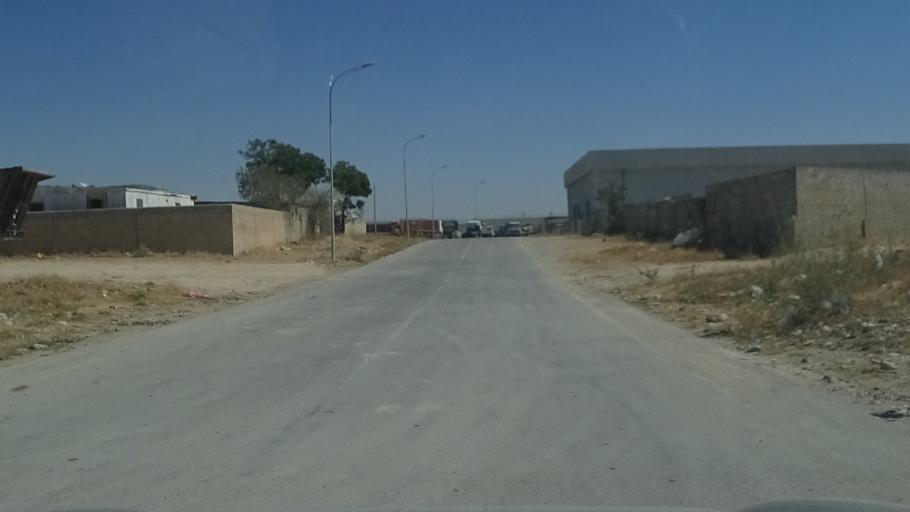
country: OM
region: Zufar
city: Salalah
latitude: 17.0335
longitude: 54.0397
